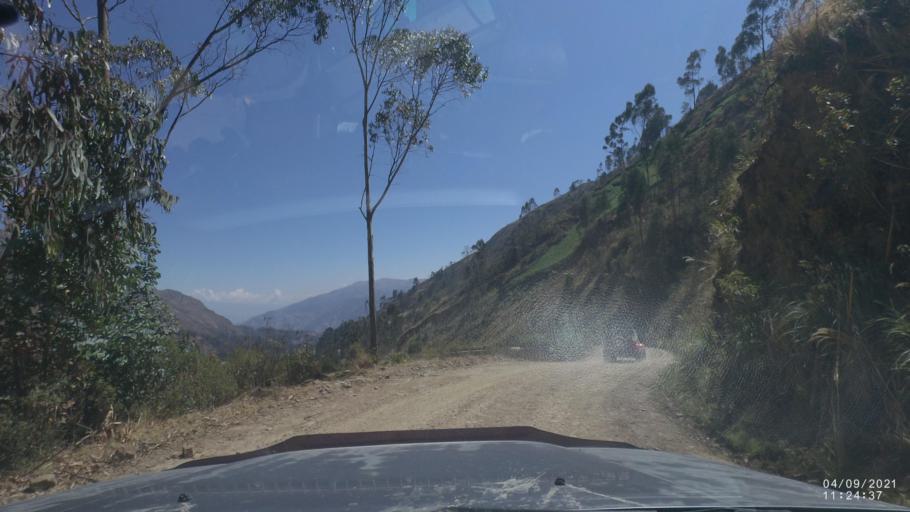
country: BO
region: Cochabamba
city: Colchani
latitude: -17.2594
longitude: -66.5099
